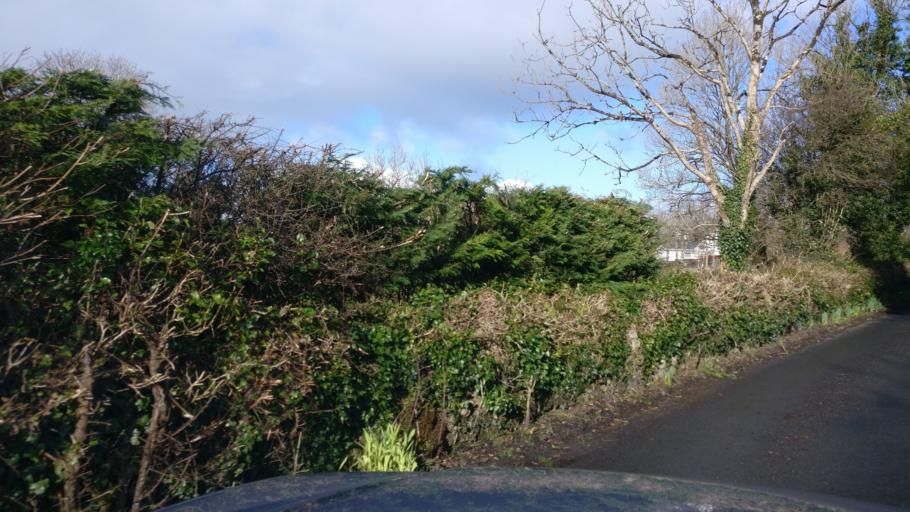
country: IE
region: Connaught
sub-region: County Galway
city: Athenry
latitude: 53.2273
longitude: -8.7447
